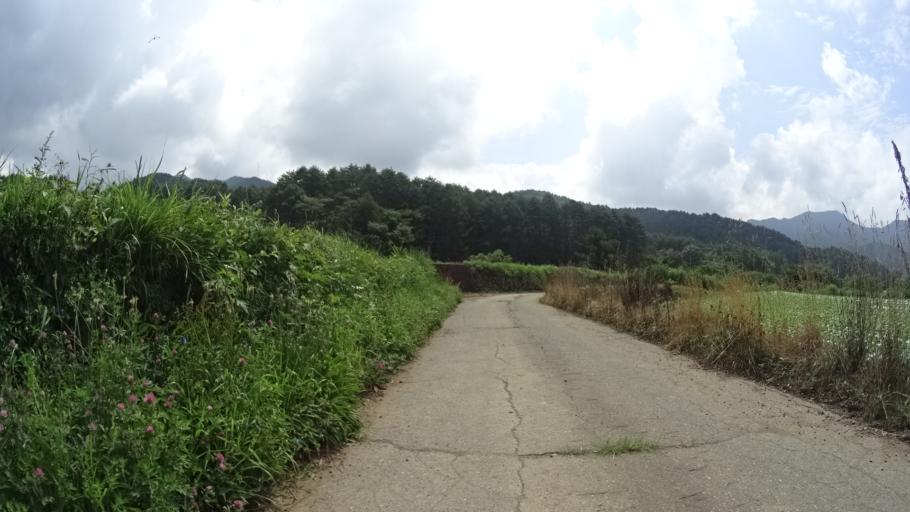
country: JP
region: Yamanashi
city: Nirasaki
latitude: 35.8974
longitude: 138.4718
